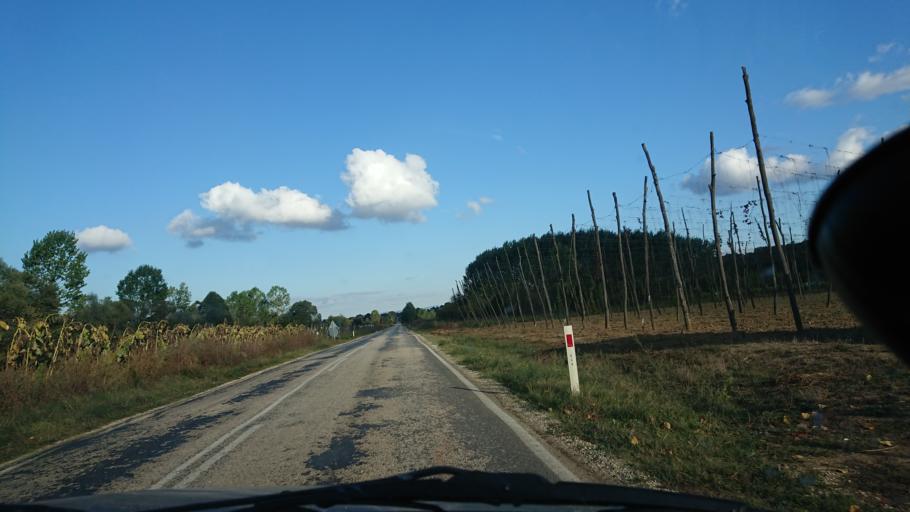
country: TR
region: Bilecik
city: Pazaryeri
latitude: 40.0161
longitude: 29.8385
